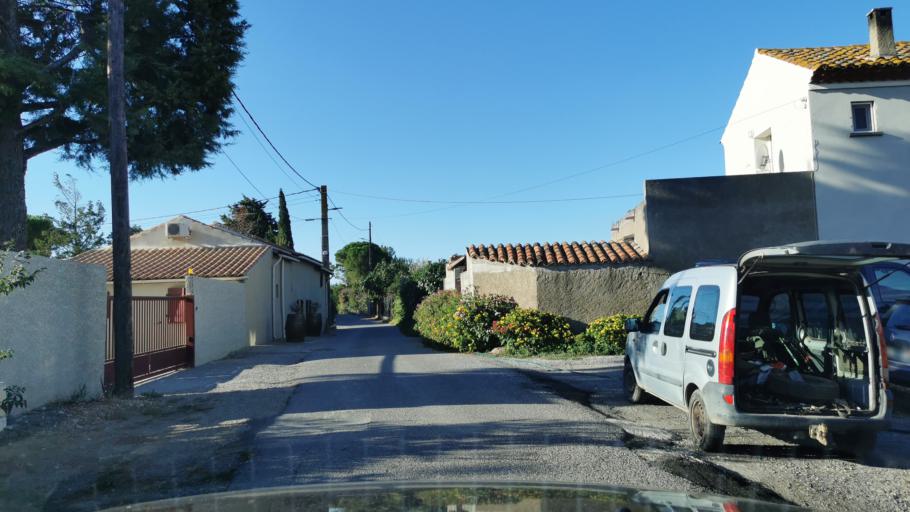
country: FR
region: Languedoc-Roussillon
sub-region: Departement de l'Aude
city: Coursan
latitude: 43.2587
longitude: 3.0215
